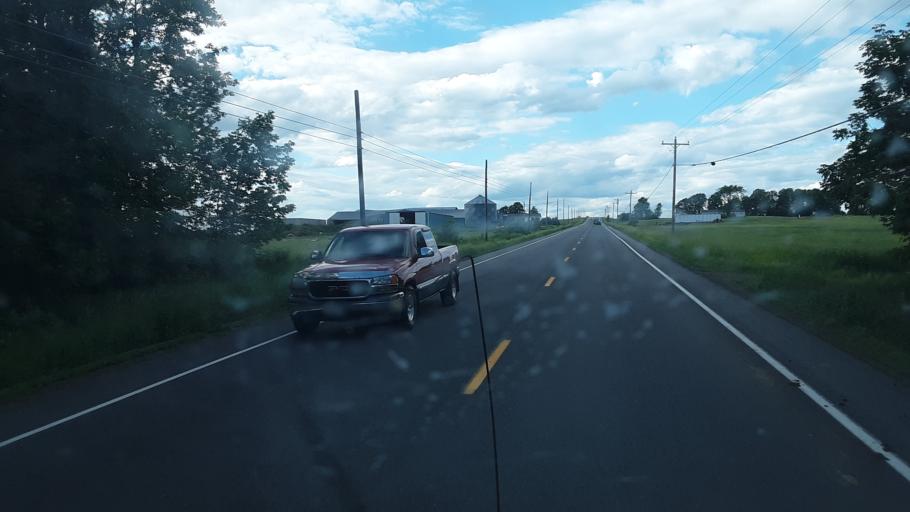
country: US
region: Maine
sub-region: Penobscot County
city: Patten
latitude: 45.9478
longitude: -68.4527
